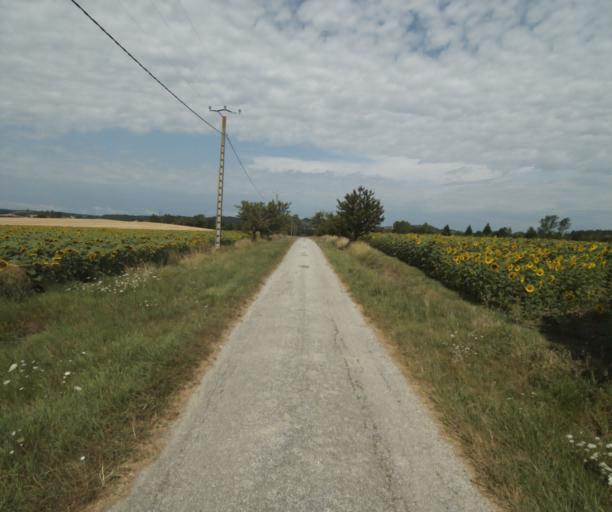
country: FR
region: Midi-Pyrenees
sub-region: Departement de la Haute-Garonne
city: Saint-Felix-Lauragais
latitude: 43.4199
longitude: 1.9136
